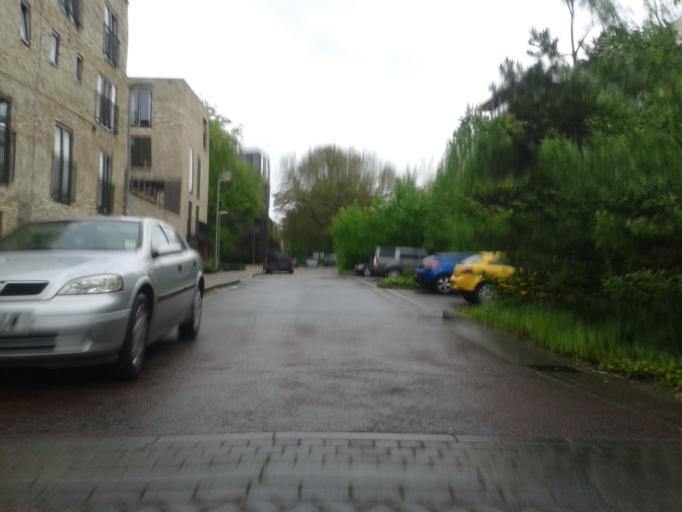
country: GB
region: England
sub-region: Cambridgeshire
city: Cambridge
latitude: 52.1885
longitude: 0.1290
